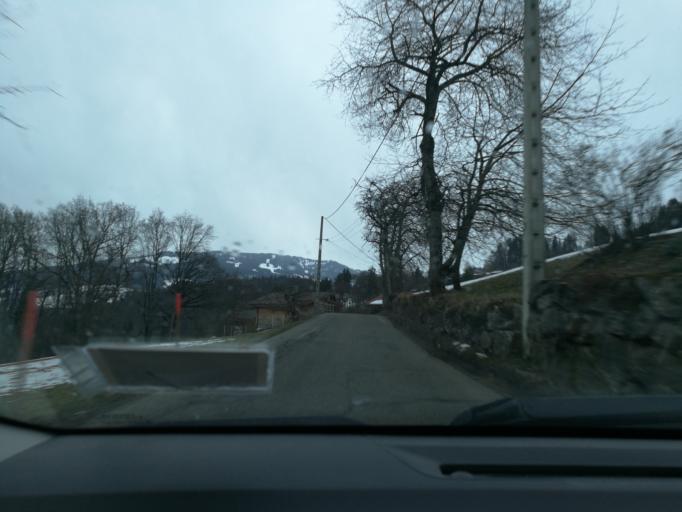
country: FR
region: Rhone-Alpes
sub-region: Departement de la Haute-Savoie
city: Domancy
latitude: 45.9135
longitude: 6.6317
